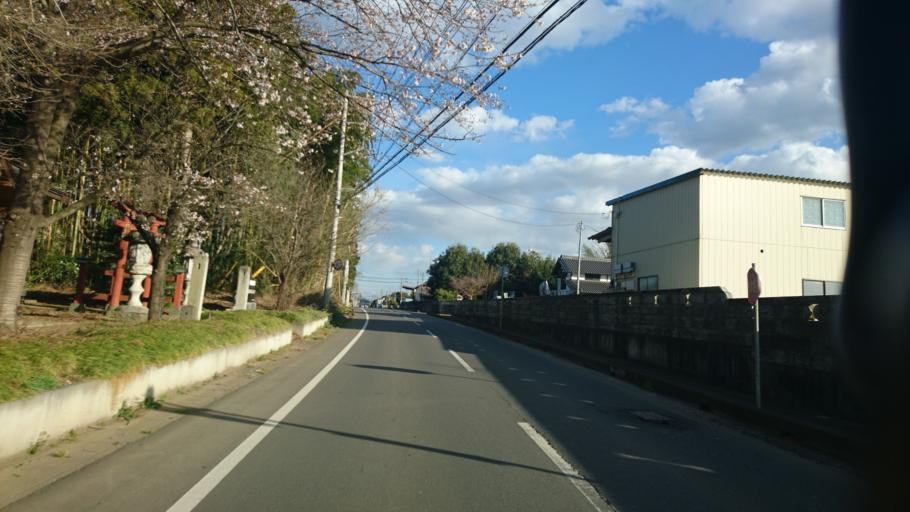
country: JP
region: Ibaraki
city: Yuki
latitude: 36.2594
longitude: 139.9236
